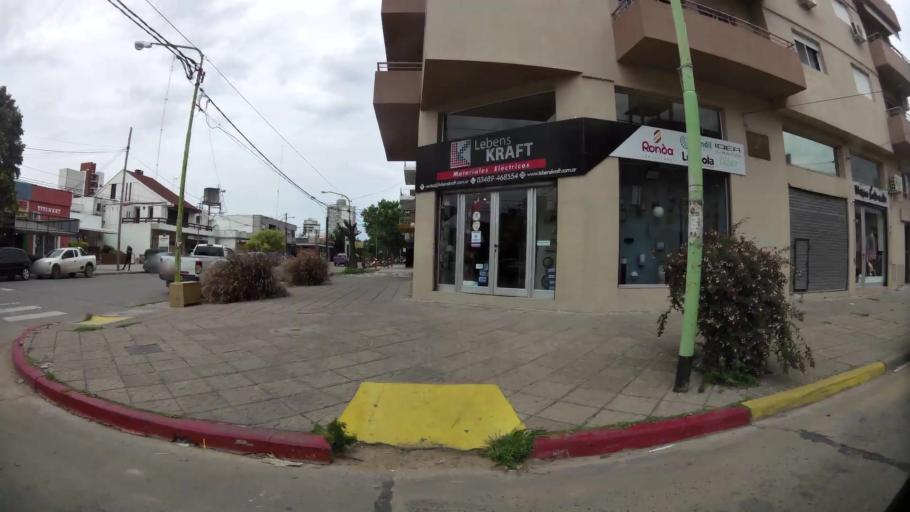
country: AR
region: Buenos Aires
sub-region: Partido de Campana
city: Campana
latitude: -34.1632
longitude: -58.9637
